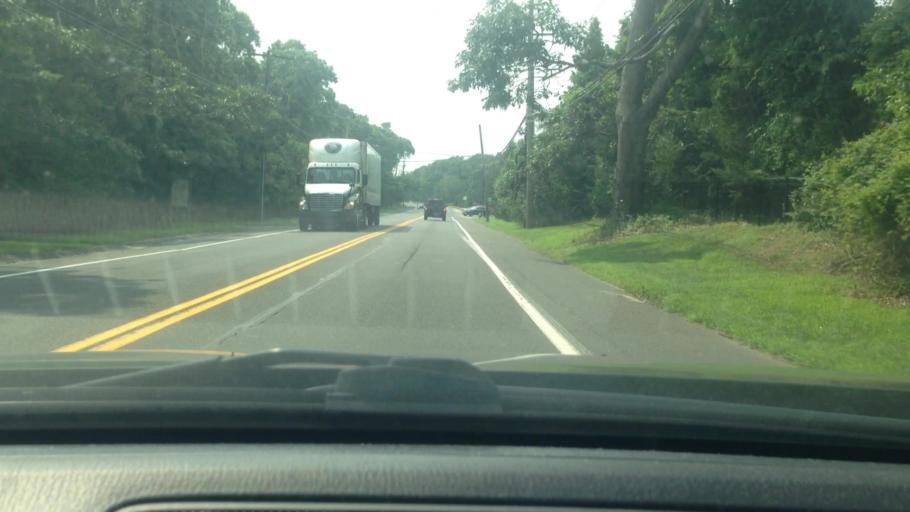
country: US
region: New York
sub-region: Suffolk County
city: Bridgehampton
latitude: 40.9668
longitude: -72.2998
